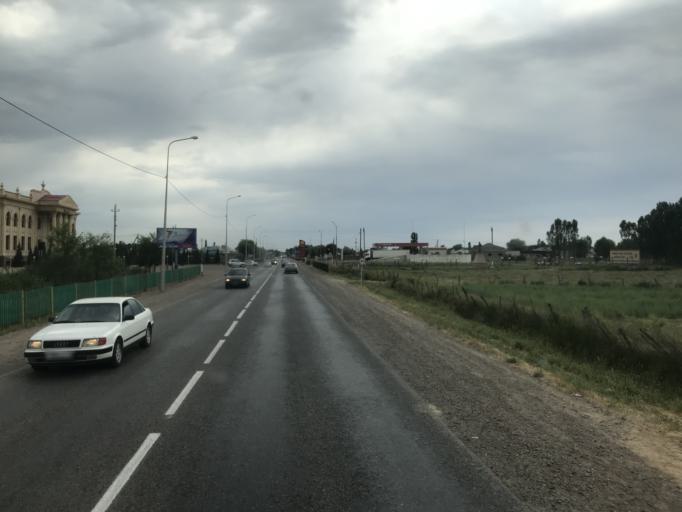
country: KZ
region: Ongtustik Qazaqstan
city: Saryaghash
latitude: 41.3548
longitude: 68.9713
